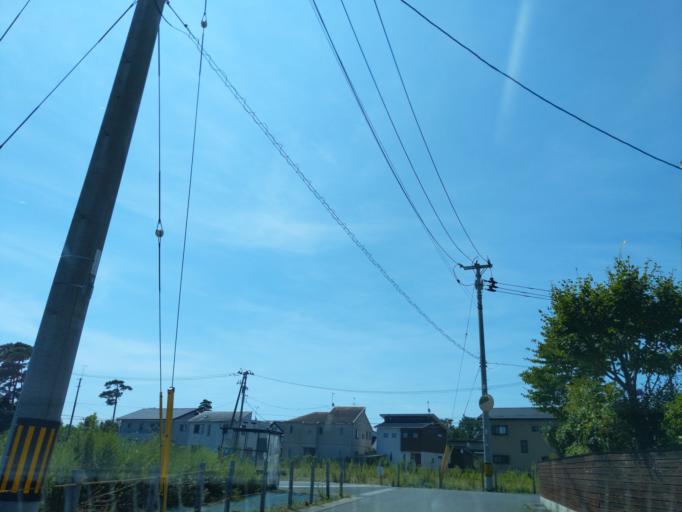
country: JP
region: Fukushima
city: Koriyama
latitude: 37.4193
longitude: 140.3661
